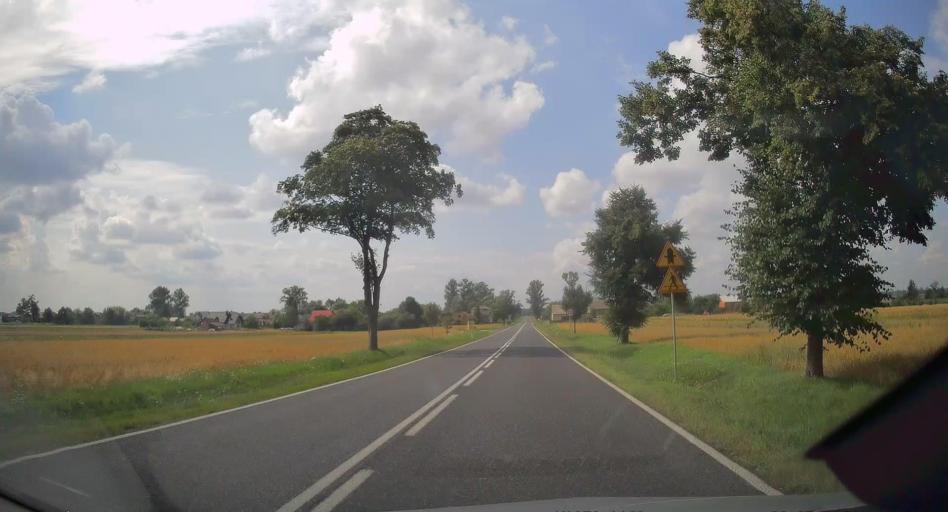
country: PL
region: Lodz Voivodeship
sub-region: Powiat skierniewicki
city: Gluchow
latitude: 51.7969
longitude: 20.0300
